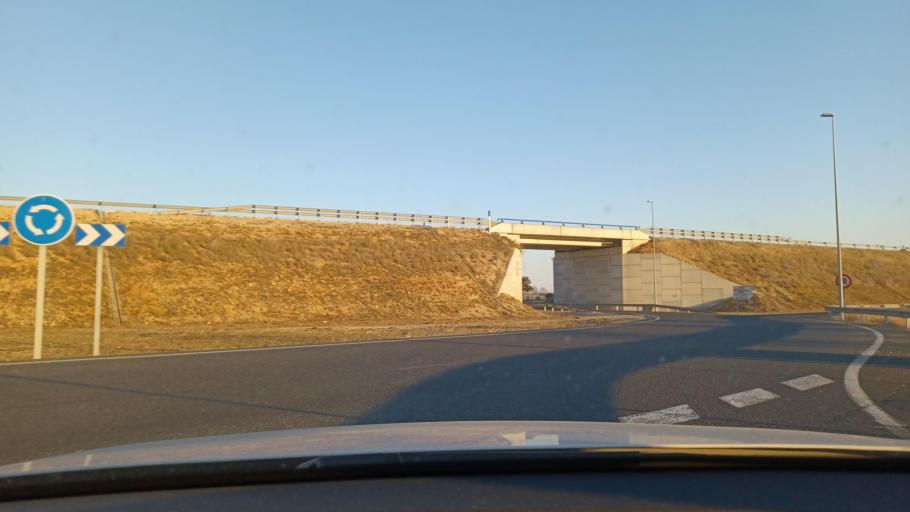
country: ES
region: Catalonia
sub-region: Provincia de Tarragona
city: Amposta
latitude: 40.7294
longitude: 0.5903
